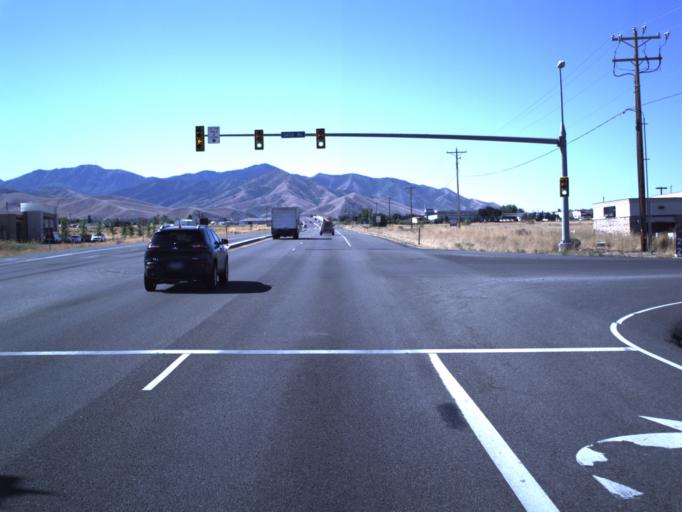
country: US
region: Utah
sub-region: Tooele County
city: Erda
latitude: 40.5732
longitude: -112.2951
